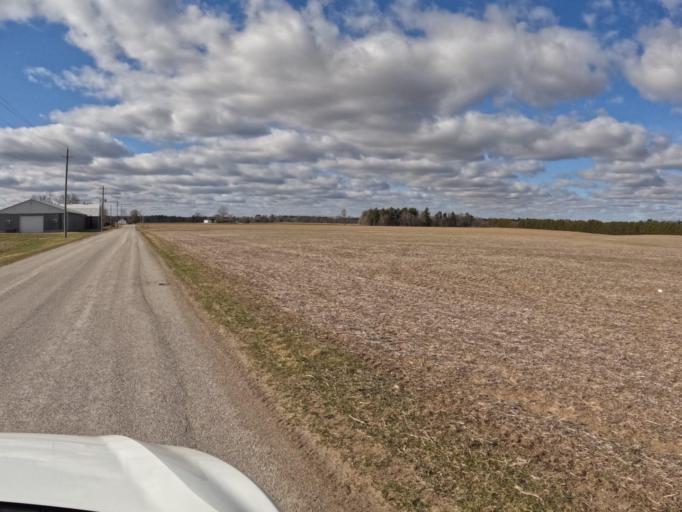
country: CA
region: Ontario
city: Norfolk County
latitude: 42.7455
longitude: -80.3823
